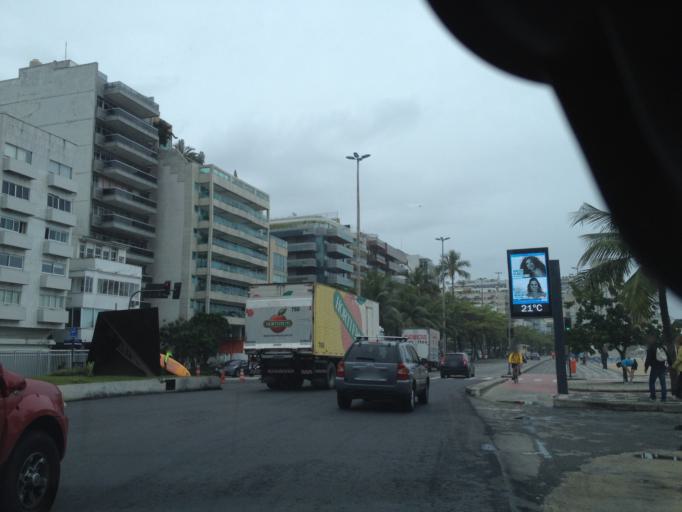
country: BR
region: Rio de Janeiro
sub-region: Rio De Janeiro
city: Rio de Janeiro
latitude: -22.9887
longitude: -43.2278
